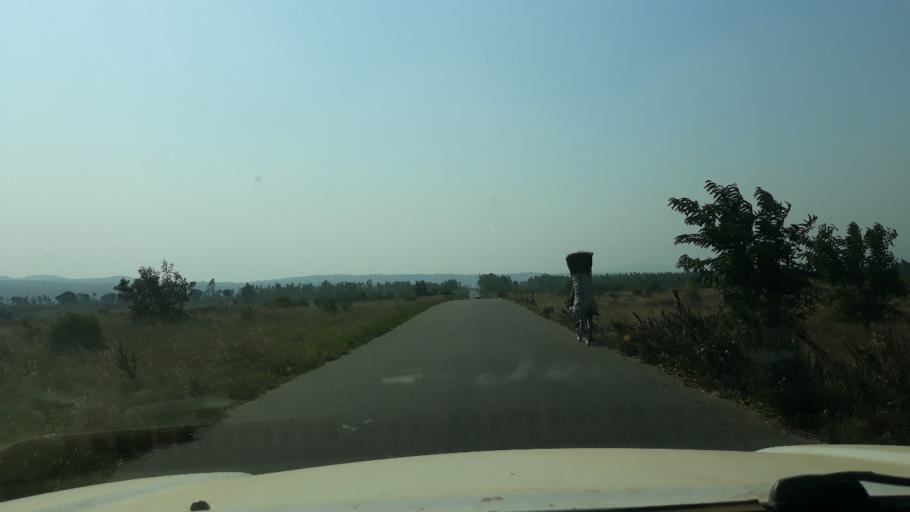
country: BI
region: Cibitoke
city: Cibitoke
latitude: -2.9425
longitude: 29.0684
